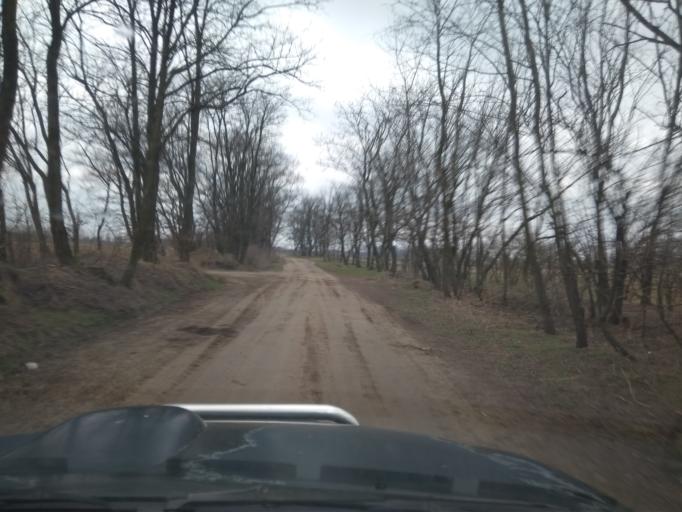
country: HU
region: Szabolcs-Szatmar-Bereg
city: Nyiregyhaza
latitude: 47.9664
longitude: 21.6642
